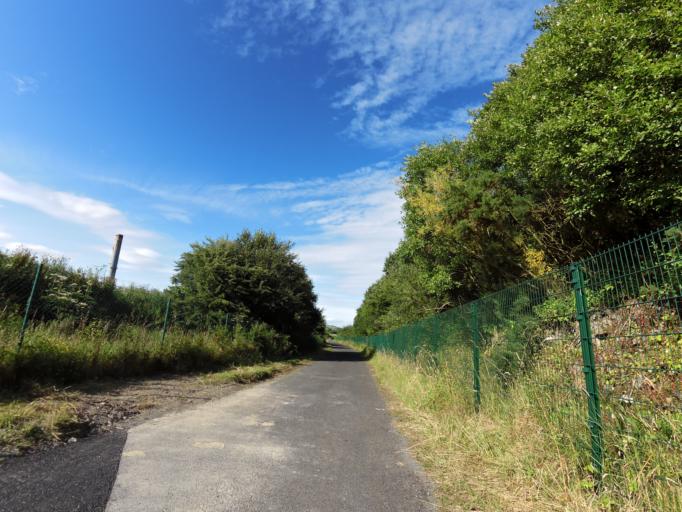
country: IE
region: Munster
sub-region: Waterford
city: Portlaw
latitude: 52.2212
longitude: -7.3440
